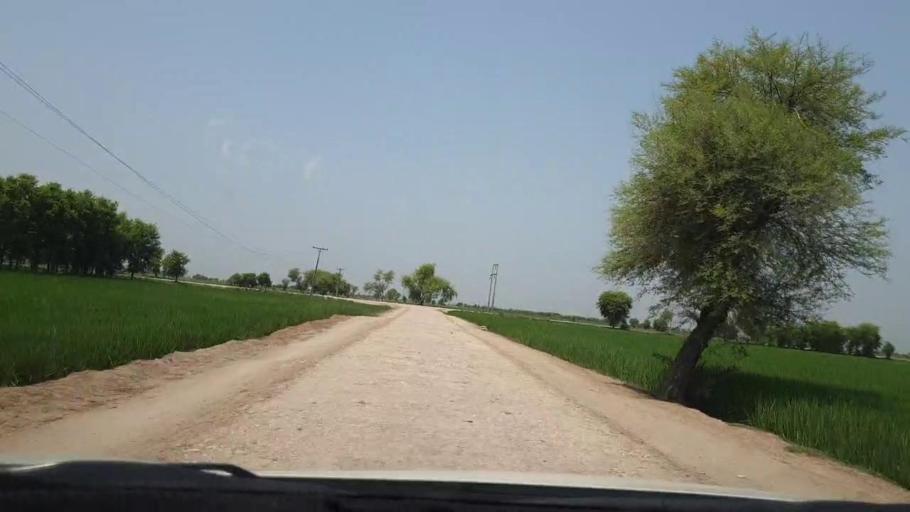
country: PK
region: Sindh
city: Radhan
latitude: 27.2494
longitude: 67.9828
